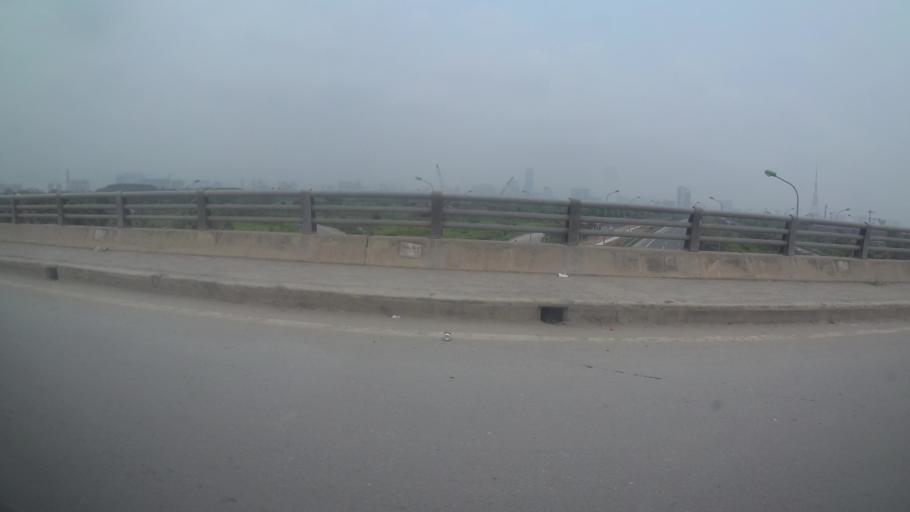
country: VN
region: Ha Noi
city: Cau Dien
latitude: 21.0097
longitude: 105.7476
